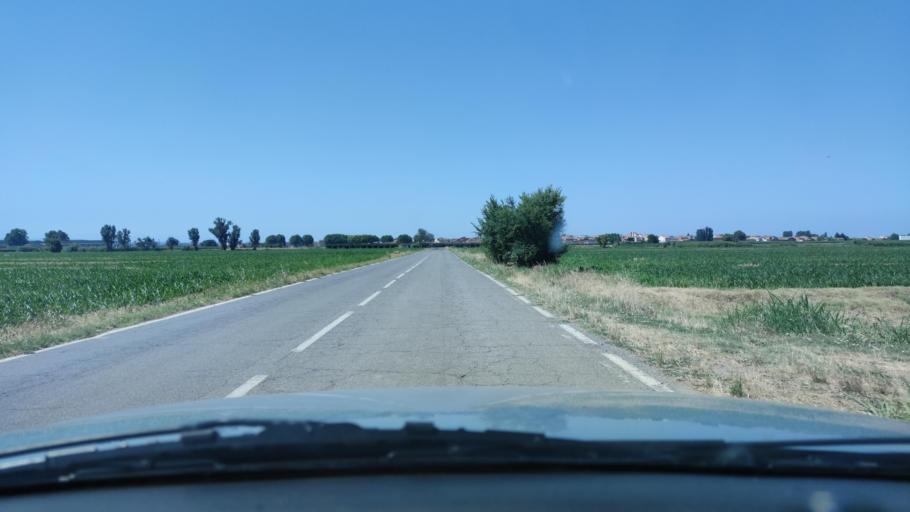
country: ES
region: Catalonia
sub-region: Provincia de Lleida
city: Mollerussa
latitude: 41.6568
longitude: 0.8920
